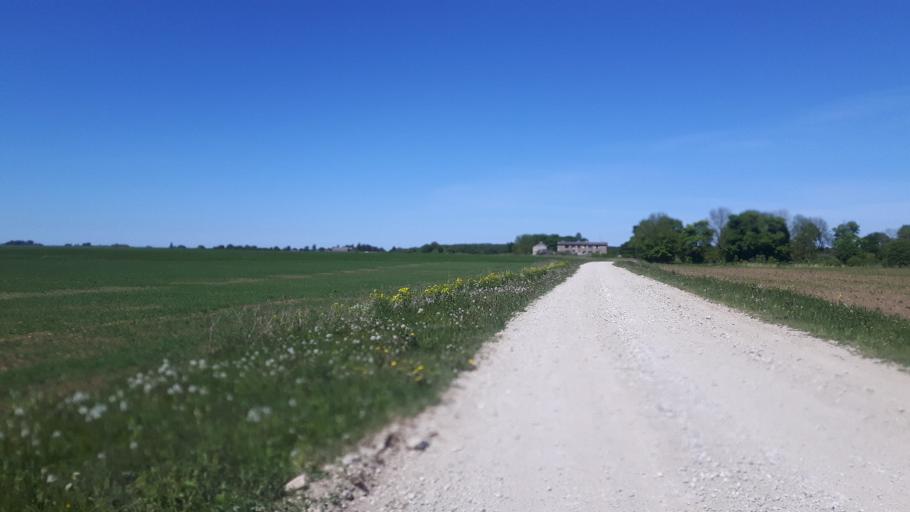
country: EE
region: Ida-Virumaa
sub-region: Toila vald
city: Voka
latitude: 59.3994
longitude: 27.6668
